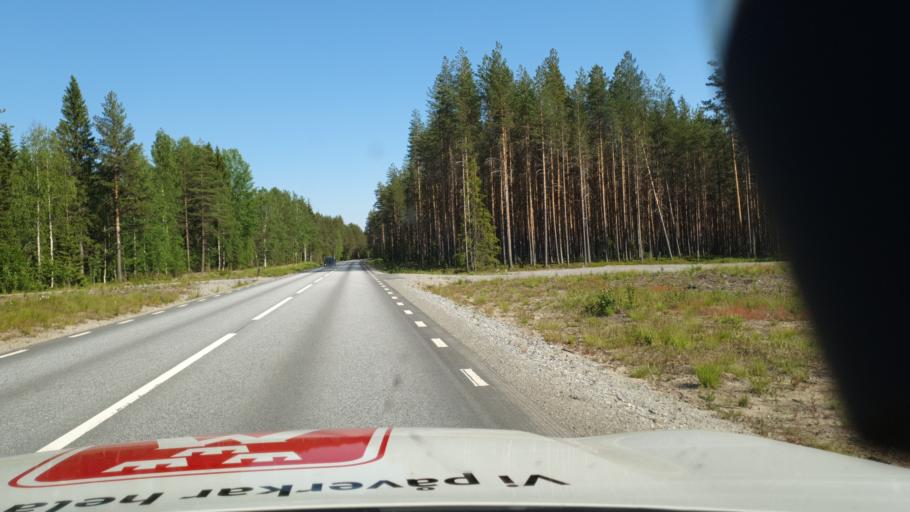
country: SE
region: Vaesterbotten
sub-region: Vindelns Kommun
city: Vindeln
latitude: 64.1746
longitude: 19.7398
